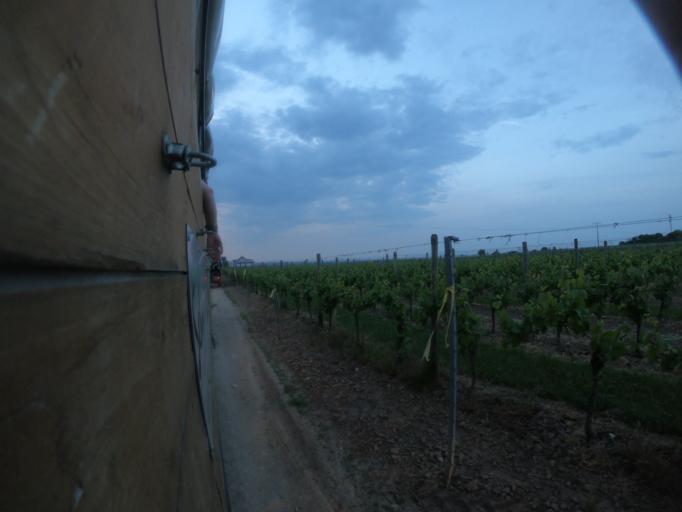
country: DE
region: Rheinland-Pfalz
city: Weinolsheim
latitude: 49.8165
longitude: 8.2782
